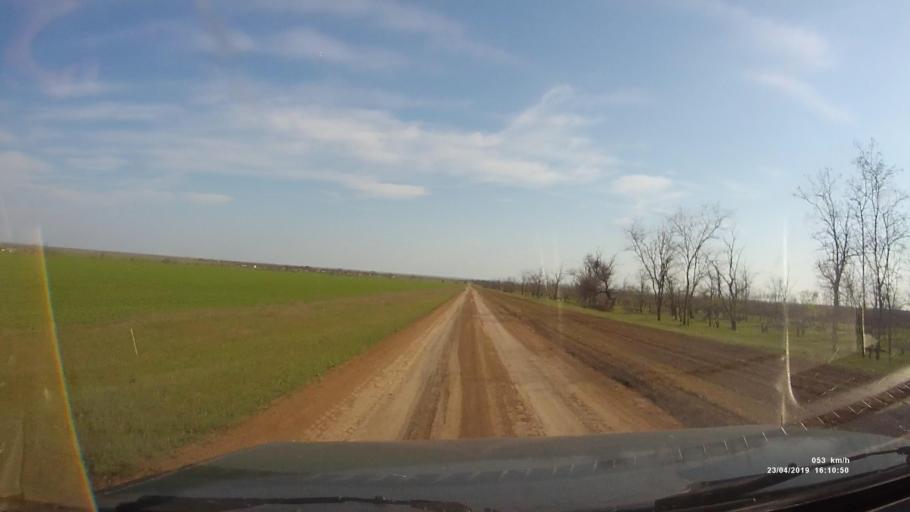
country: RU
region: Rostov
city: Remontnoye
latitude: 46.4790
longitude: 43.1231
